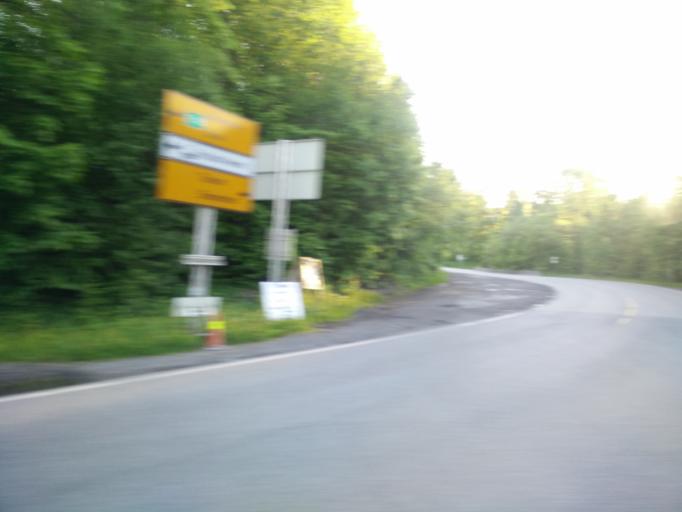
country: NO
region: Akershus
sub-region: Baerum
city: Sandvika
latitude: 59.8928
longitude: 10.5099
